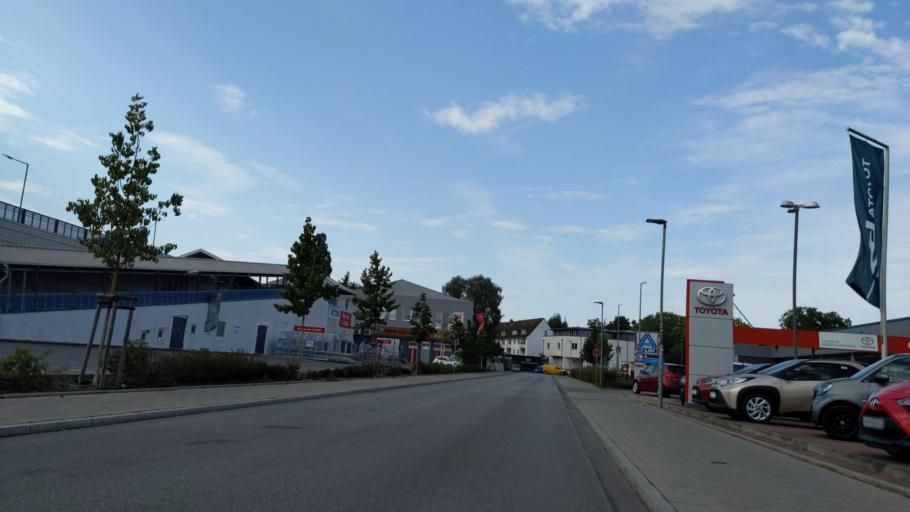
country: DE
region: Schleswig-Holstein
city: Luebeck
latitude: 53.8661
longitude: 10.7216
